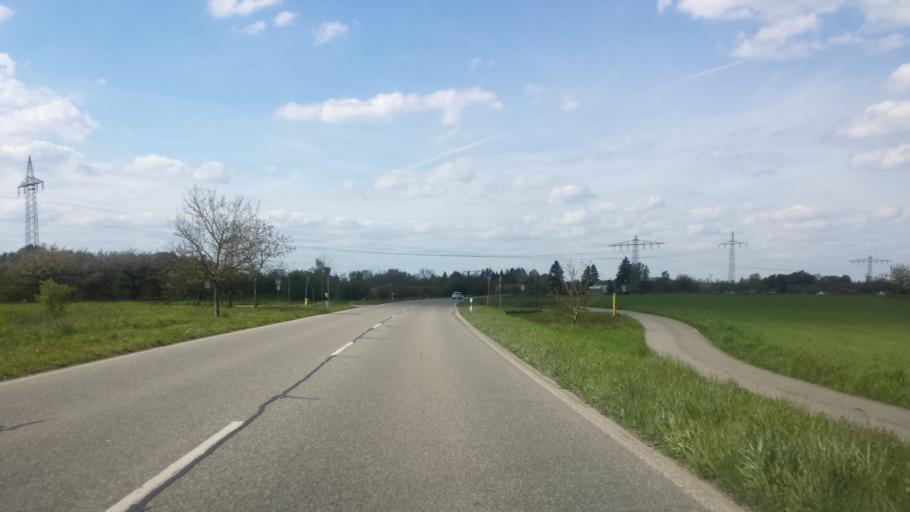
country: DE
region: Baden-Wuerttemberg
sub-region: Karlsruhe Region
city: Weingarten
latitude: 49.0630
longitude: 8.4816
